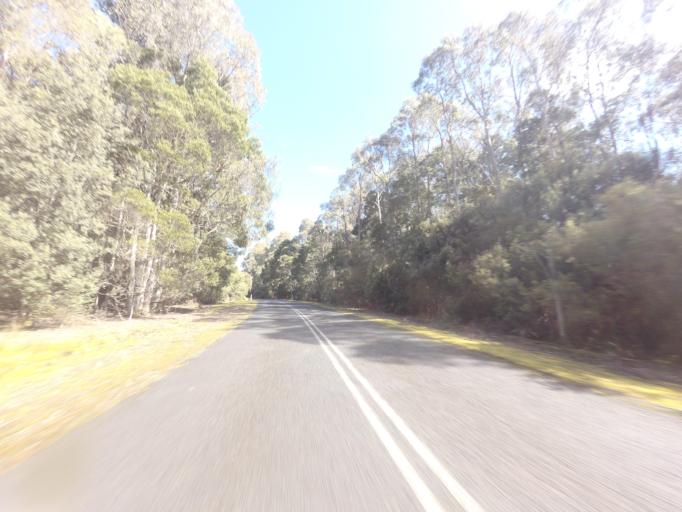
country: AU
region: Tasmania
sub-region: Derwent Valley
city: New Norfolk
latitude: -42.7630
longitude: 146.5364
